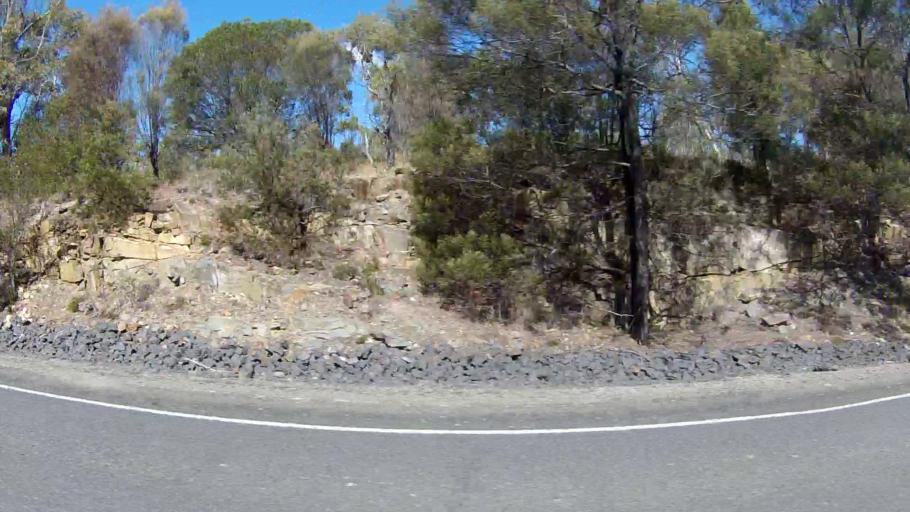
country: AU
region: Tasmania
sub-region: Sorell
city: Sorell
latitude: -42.5862
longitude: 147.8014
